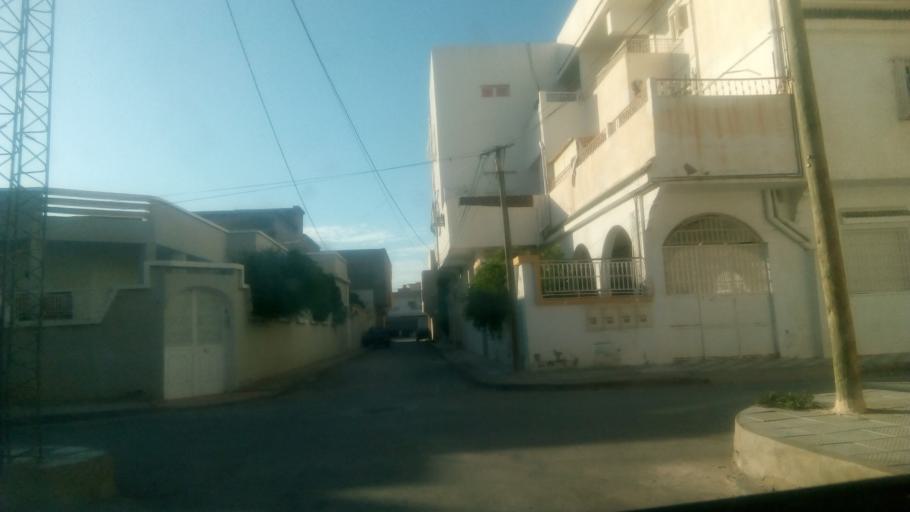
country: TN
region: Al Qayrawan
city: Kairouan
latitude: 35.6687
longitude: 10.0814
